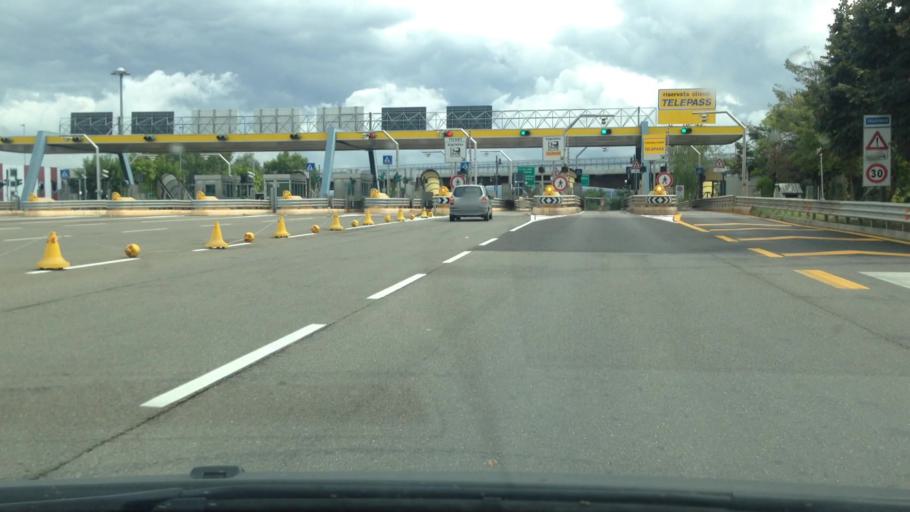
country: IT
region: Piedmont
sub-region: Provincia di Alessandria
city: Tortona
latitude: 44.9093
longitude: 8.8384
